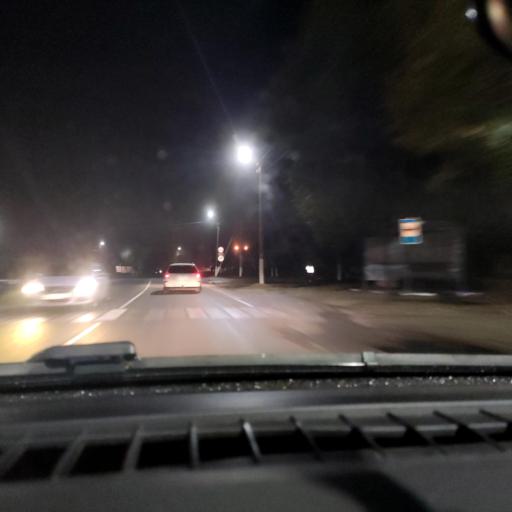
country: RU
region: Voronezj
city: Novaya Usman'
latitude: 51.6371
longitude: 39.4050
